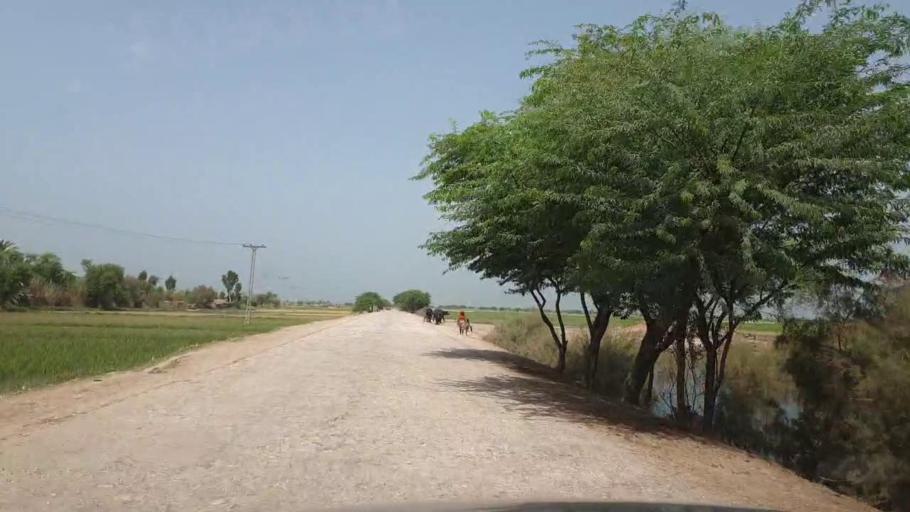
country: PK
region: Sindh
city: Garhi Yasin
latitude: 27.8575
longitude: 68.4149
